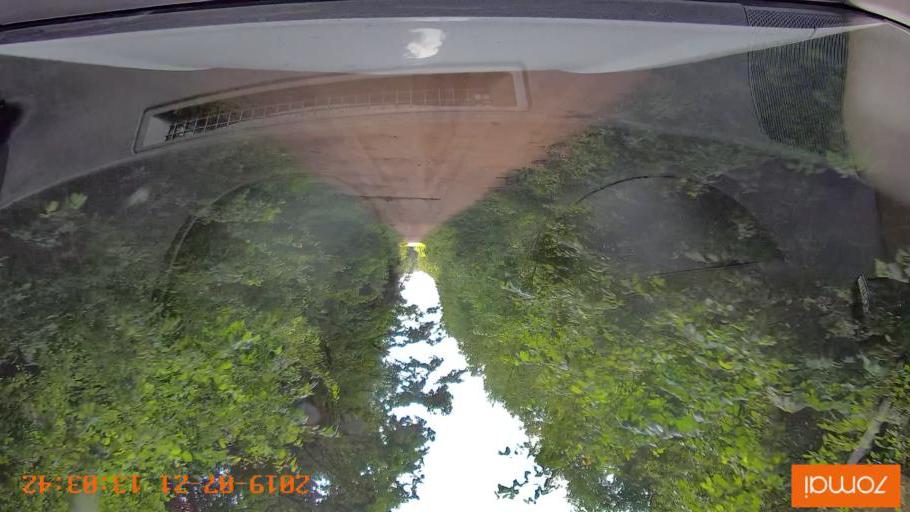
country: BY
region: Grodnenskaya
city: Lyubcha
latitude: 53.8407
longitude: 26.0248
